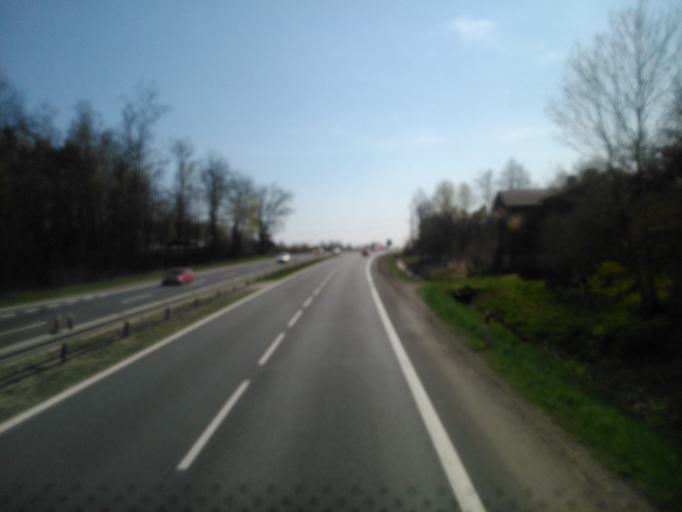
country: PL
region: Silesian Voivodeship
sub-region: Powiat czestochowski
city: Kamienica Polska
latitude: 50.6429
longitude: 19.1354
